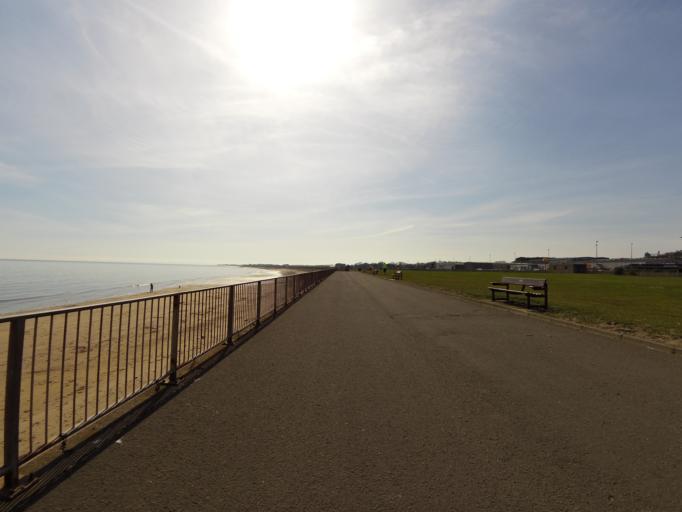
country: GB
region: Scotland
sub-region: Angus
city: Arbroath
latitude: 56.5499
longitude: -2.6076
